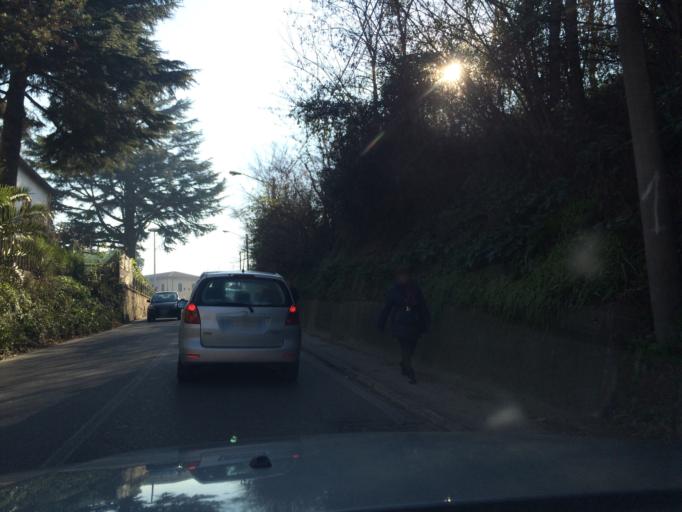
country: IT
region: Umbria
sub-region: Provincia di Terni
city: Terni
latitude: 42.5560
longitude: 12.6586
